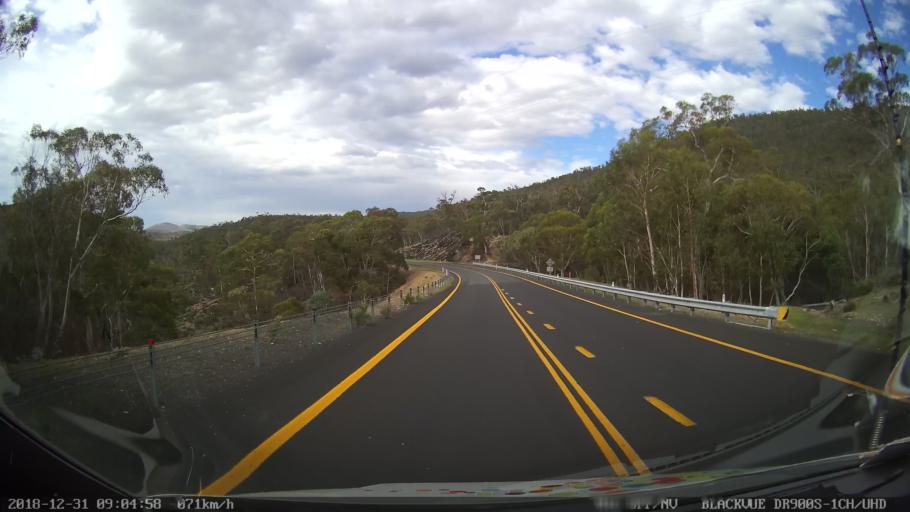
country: AU
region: New South Wales
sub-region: Snowy River
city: Jindabyne
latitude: -36.3588
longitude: 148.5890
